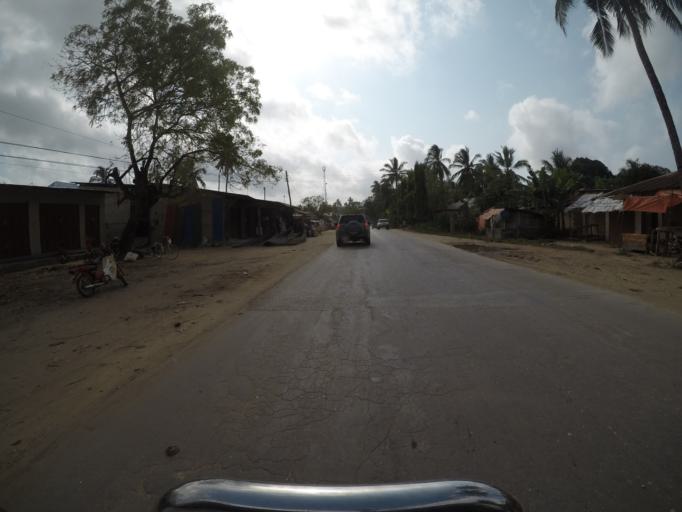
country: TZ
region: Zanzibar Central/South
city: Koani
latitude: -6.1953
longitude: 39.2828
